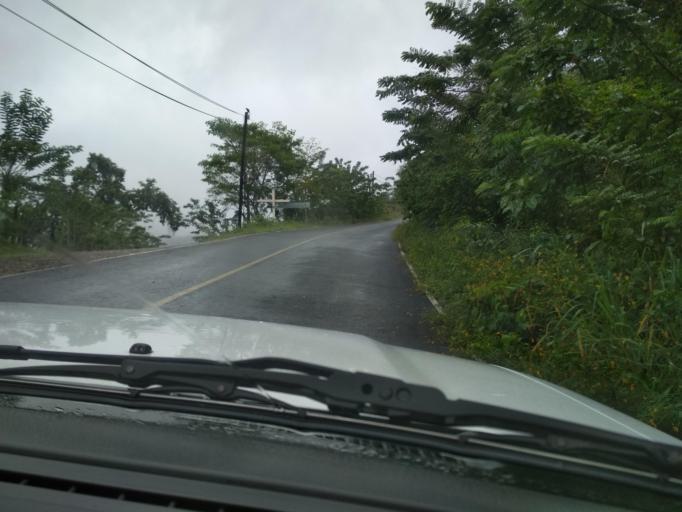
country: MX
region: Veracruz
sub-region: Chalma
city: San Pedro Coyutla
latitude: 21.2304
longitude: -98.4507
